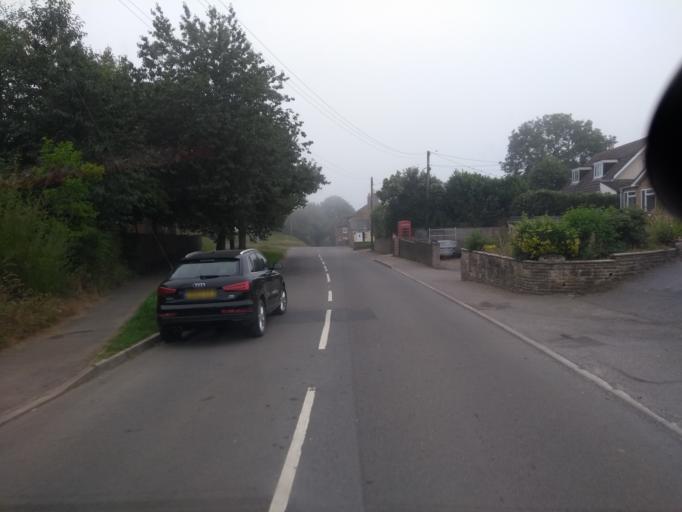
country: GB
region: England
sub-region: Dorset
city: Bridport
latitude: 50.7667
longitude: -2.7734
